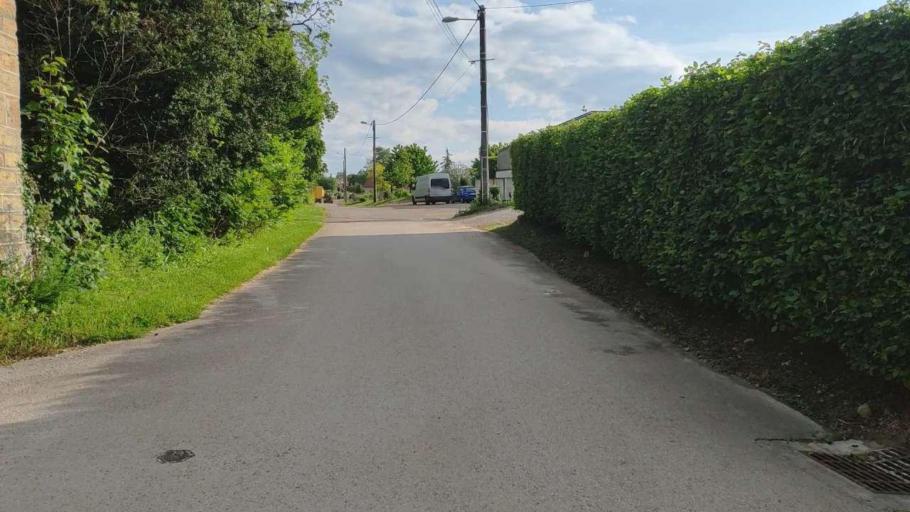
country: FR
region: Franche-Comte
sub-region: Departement du Jura
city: Perrigny
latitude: 46.7316
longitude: 5.5943
